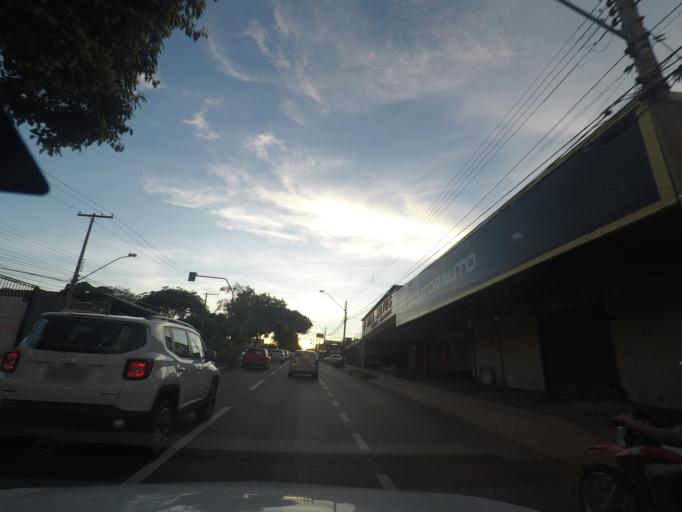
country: BR
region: Goias
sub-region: Goiania
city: Goiania
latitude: -16.6949
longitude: -49.2942
